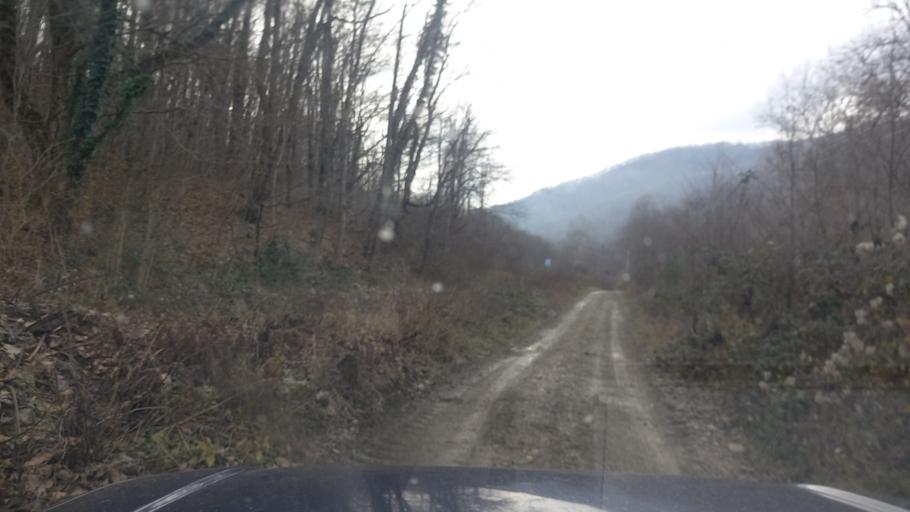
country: RU
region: Krasnodarskiy
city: Neftegorsk
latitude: 44.2164
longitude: 39.7182
